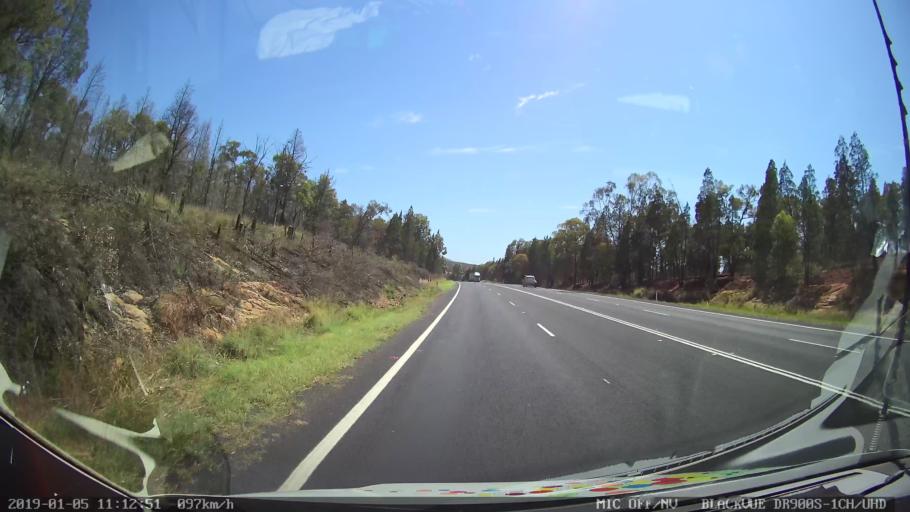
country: AU
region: New South Wales
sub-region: Warrumbungle Shire
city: Coonabarabran
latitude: -31.3776
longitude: 149.2652
